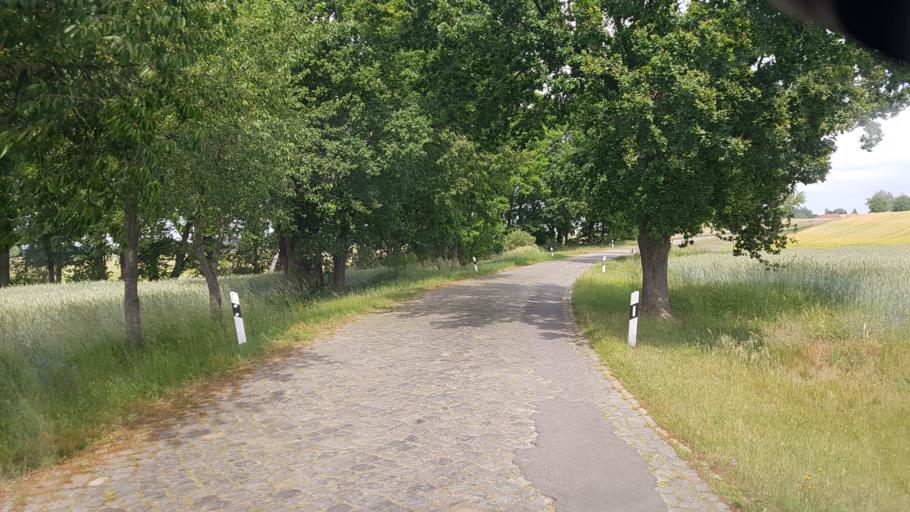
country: DE
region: Brandenburg
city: Lebusa
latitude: 51.8086
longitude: 13.4455
